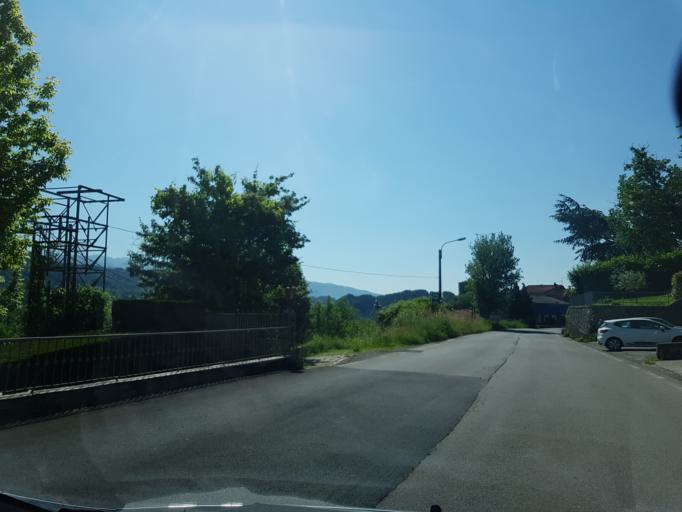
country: IT
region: Tuscany
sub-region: Provincia di Lucca
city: Camporgiano
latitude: 44.1616
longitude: 10.3316
